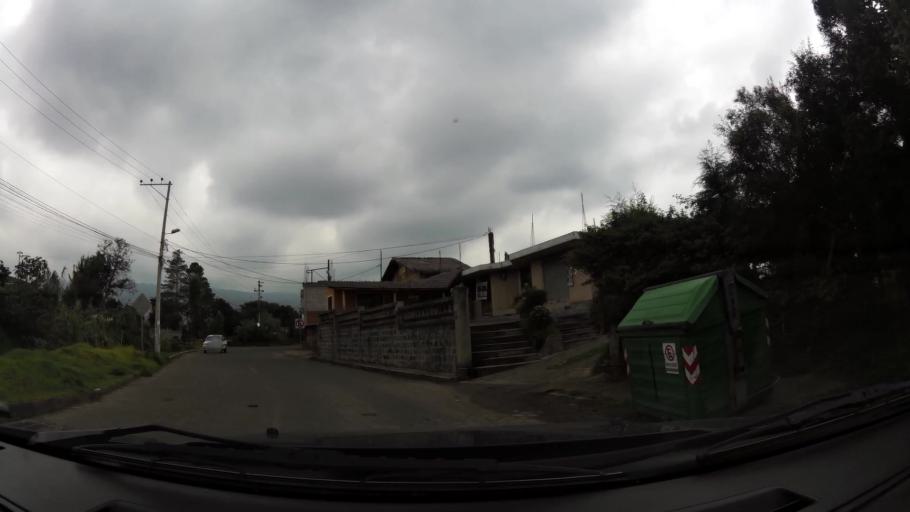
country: EC
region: Pichincha
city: Sangolqui
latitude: -0.3314
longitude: -78.4727
